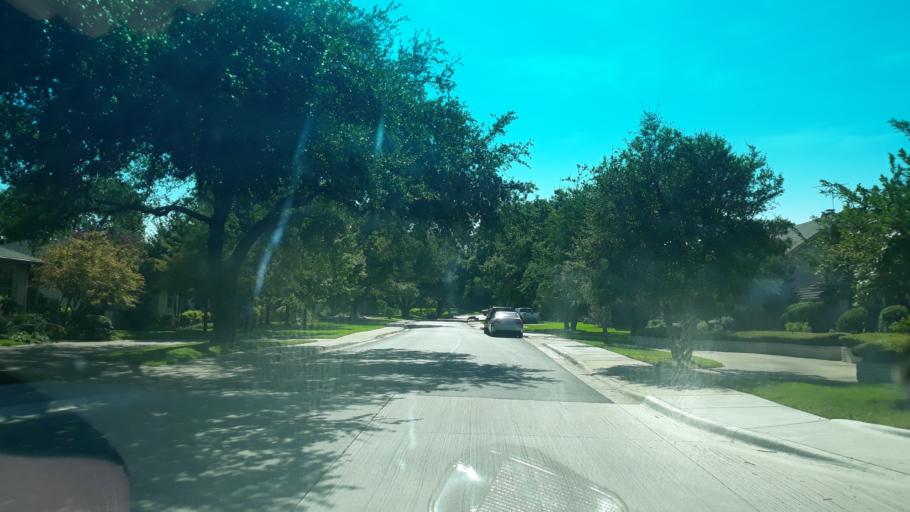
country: US
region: Texas
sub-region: Dallas County
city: Highland Park
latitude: 32.8213
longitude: -96.7465
